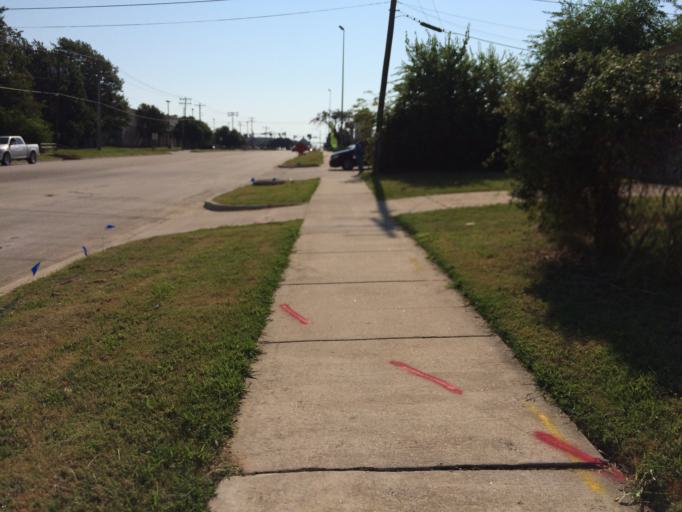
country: US
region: Oklahoma
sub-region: Cleveland County
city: Norman
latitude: 35.2182
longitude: -97.4265
